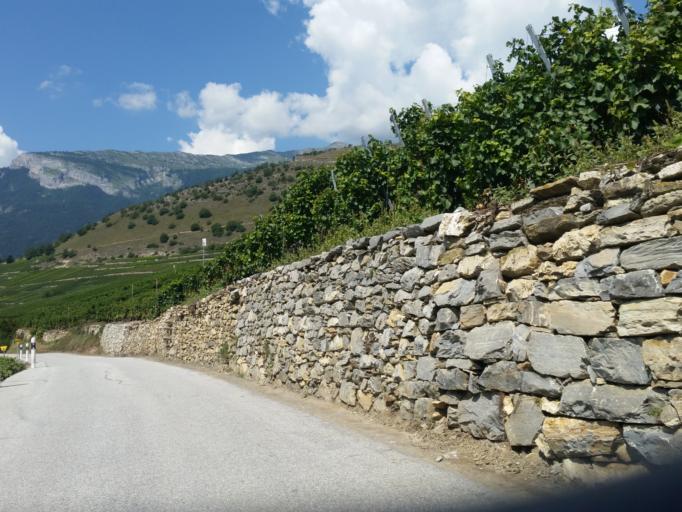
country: CH
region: Valais
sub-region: Sion District
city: Saviese
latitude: 46.2360
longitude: 7.3307
